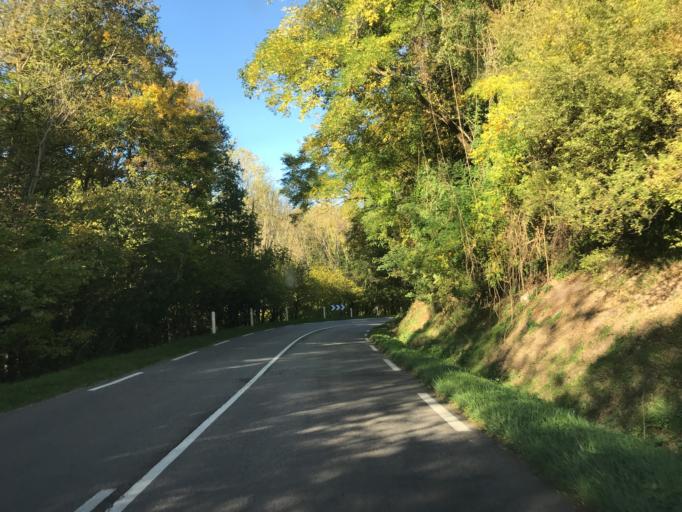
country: FR
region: Haute-Normandie
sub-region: Departement de l'Eure
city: Saint-Aubin-sur-Gaillon
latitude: 49.0847
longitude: 1.2634
